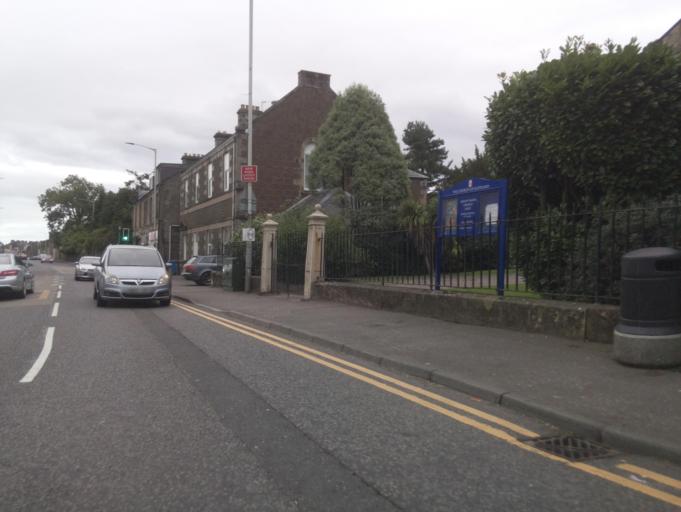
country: GB
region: Scotland
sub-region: Fife
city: Leslie
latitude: 56.2005
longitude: -3.2159
